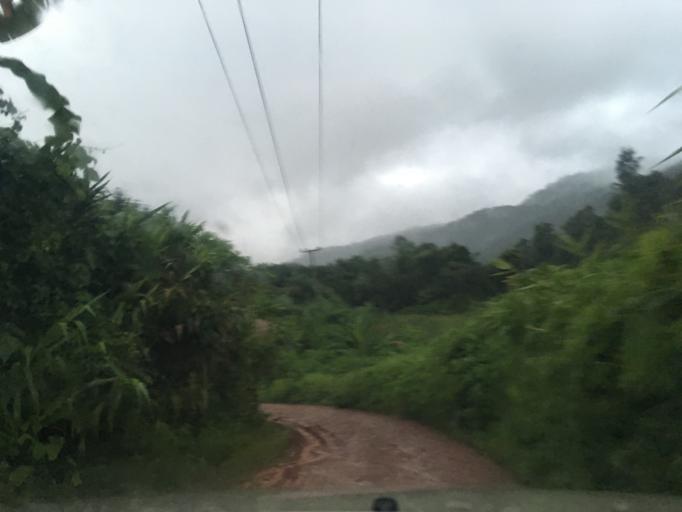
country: LA
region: Oudomxai
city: Muang La
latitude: 21.2480
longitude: 101.9337
